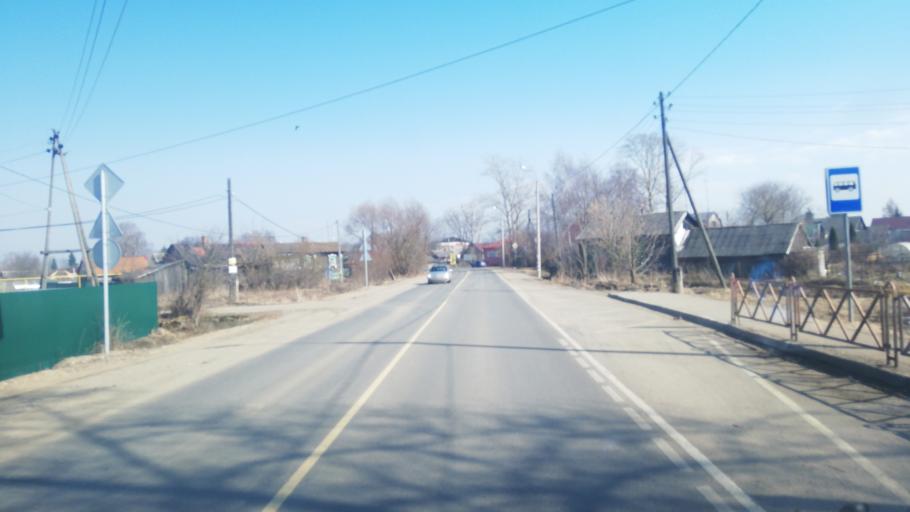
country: RU
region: Jaroslavl
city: Semibratovo
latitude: 57.2323
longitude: 39.4974
